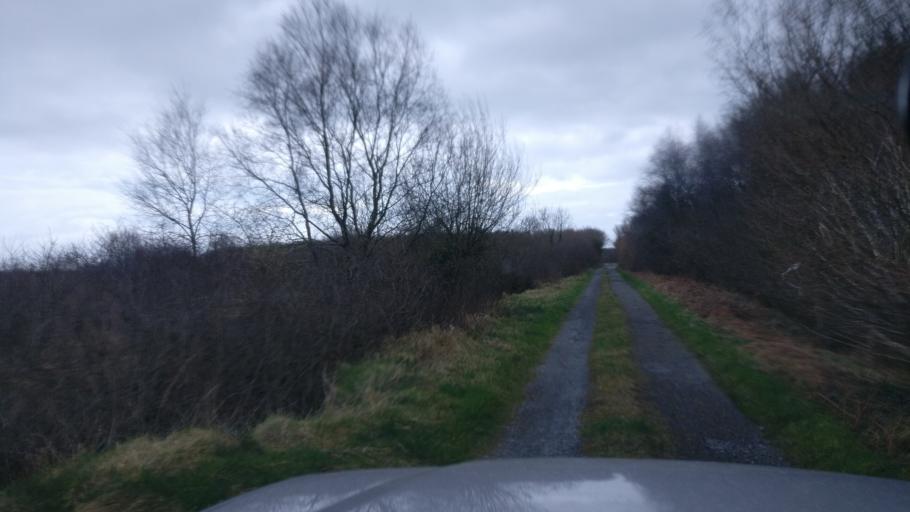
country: IE
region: Connaught
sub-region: County Galway
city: Loughrea
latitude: 53.2742
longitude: -8.4571
